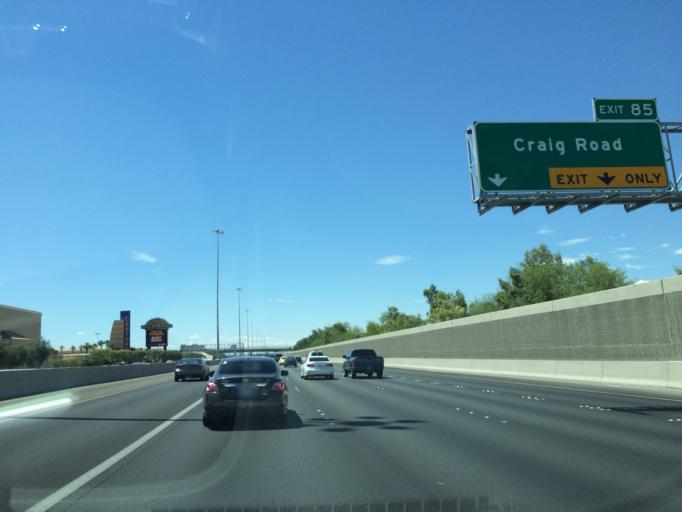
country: US
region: Nevada
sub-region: Clark County
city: Las Vegas
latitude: 36.2524
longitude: -115.2469
